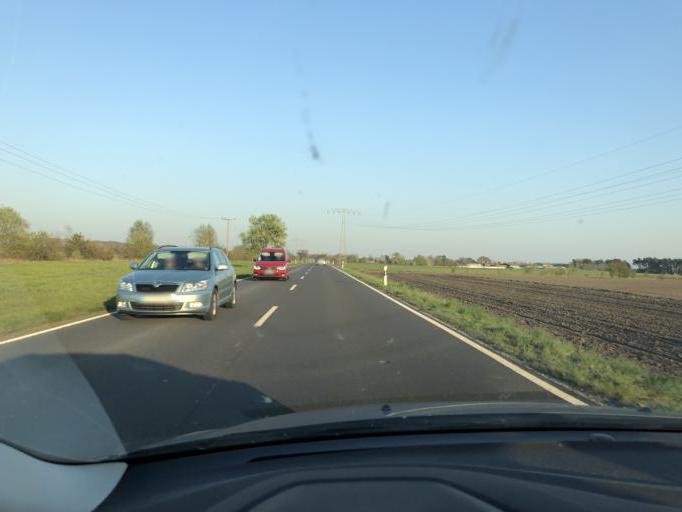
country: DE
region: Brandenburg
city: Welzow
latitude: 51.5330
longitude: 14.2042
